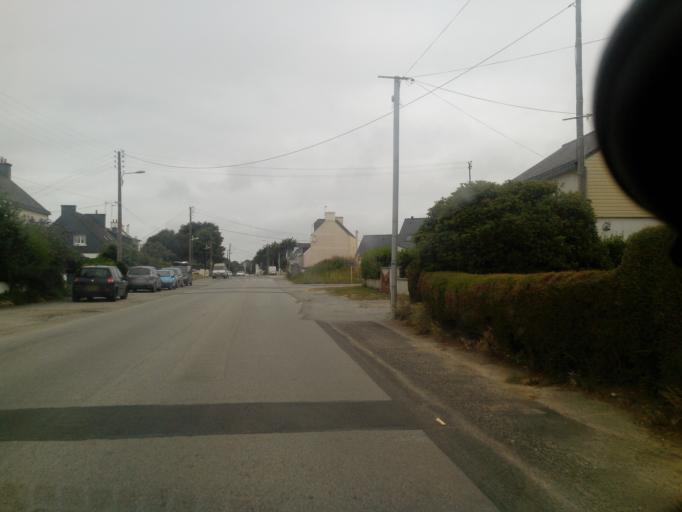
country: FR
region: Brittany
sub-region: Departement du Morbihan
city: Merlevenez
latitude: 47.6999
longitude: -3.2559
